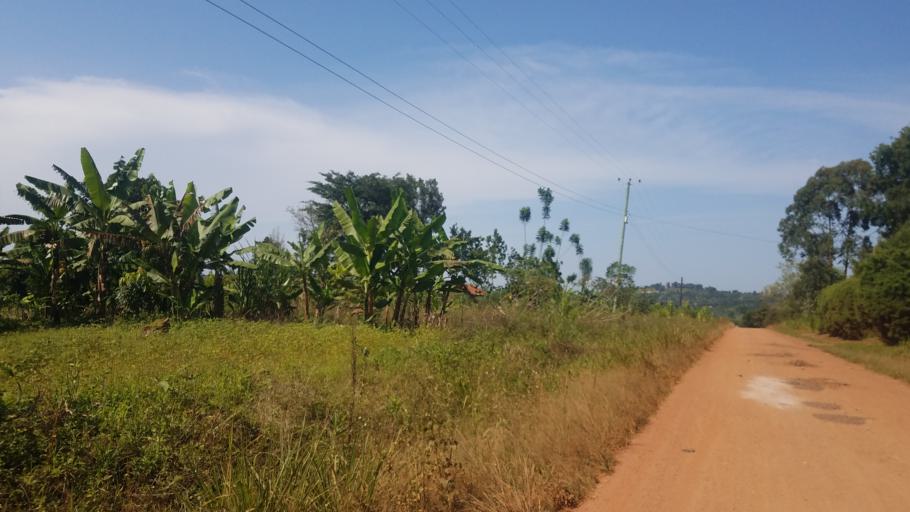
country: UG
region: Central Region
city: Masaka
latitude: -0.3090
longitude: 31.6825
